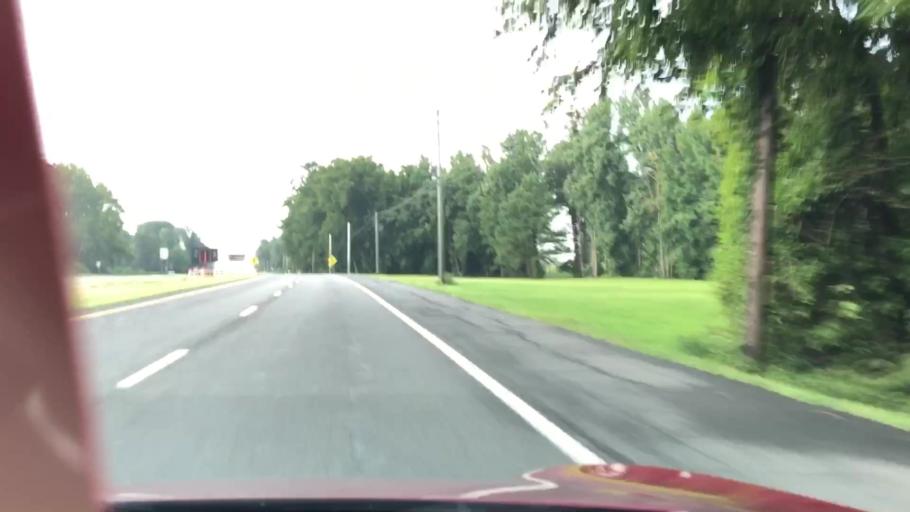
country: US
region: Delaware
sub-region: Kent County
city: Felton
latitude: 38.9744
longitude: -75.5673
